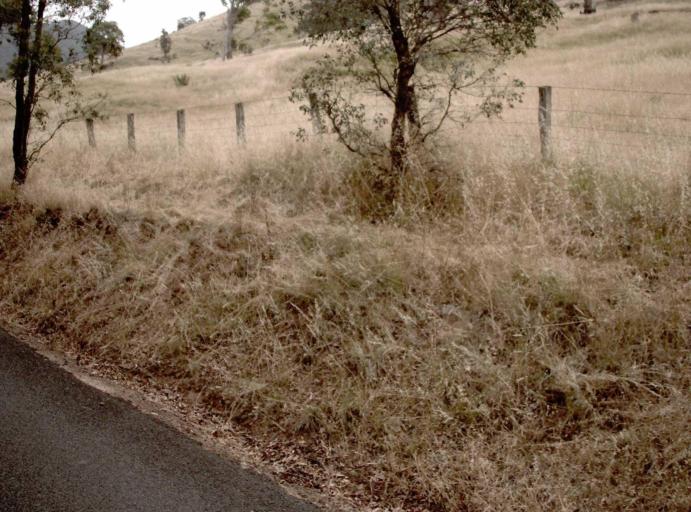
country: AU
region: Victoria
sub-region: Wellington
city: Heyfield
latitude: -37.6814
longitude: 146.6561
